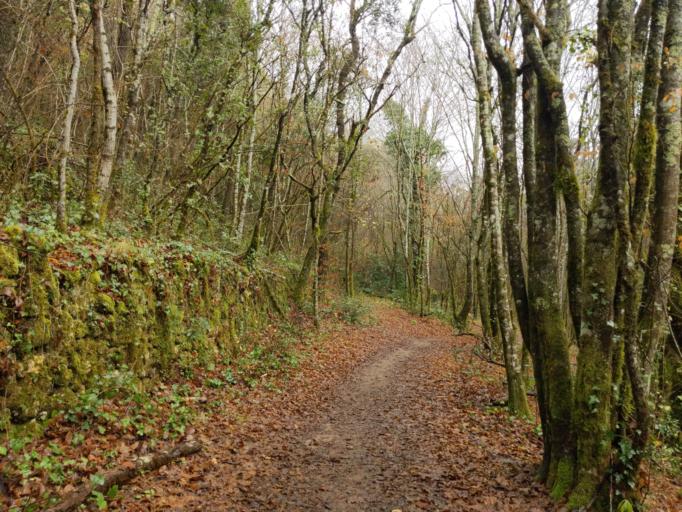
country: FR
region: Provence-Alpes-Cote d'Azur
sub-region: Departement du Var
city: Bagnols-en-Foret
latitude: 43.5406
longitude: 6.6996
